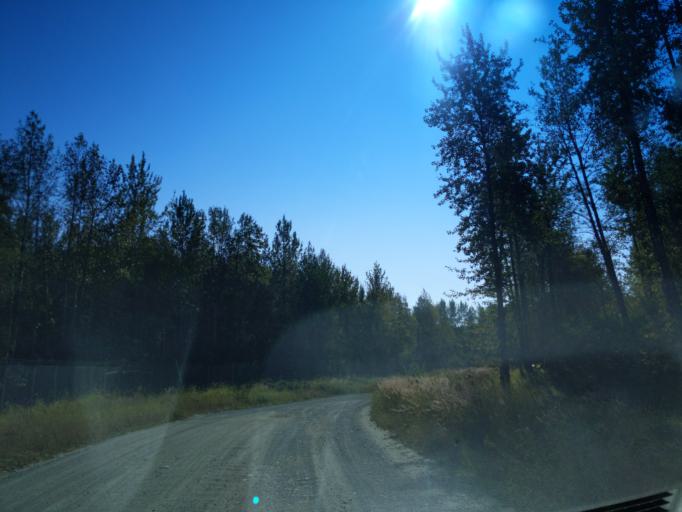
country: US
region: Alaska
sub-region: Anchorage Municipality
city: Anchorage
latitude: 61.1605
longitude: -150.0121
